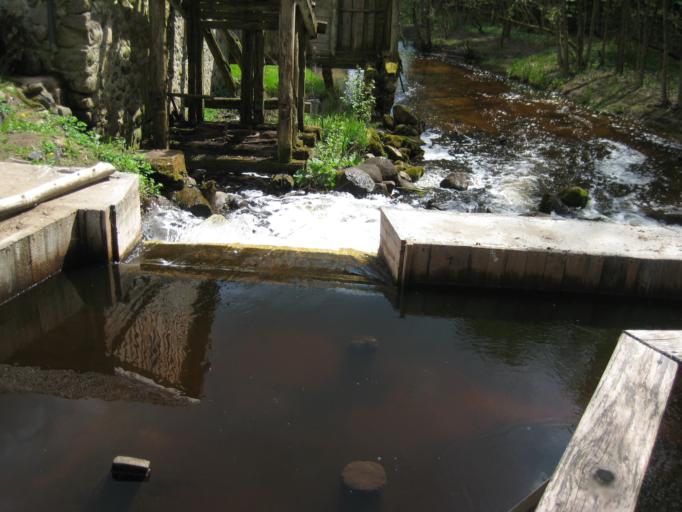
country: LT
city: Zarasai
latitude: 55.7337
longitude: 26.1980
